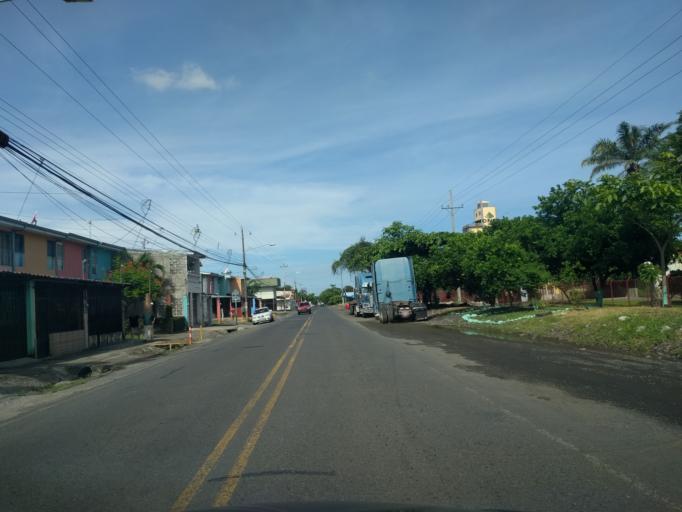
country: CR
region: Puntarenas
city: Esparza
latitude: 9.9889
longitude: -84.7135
